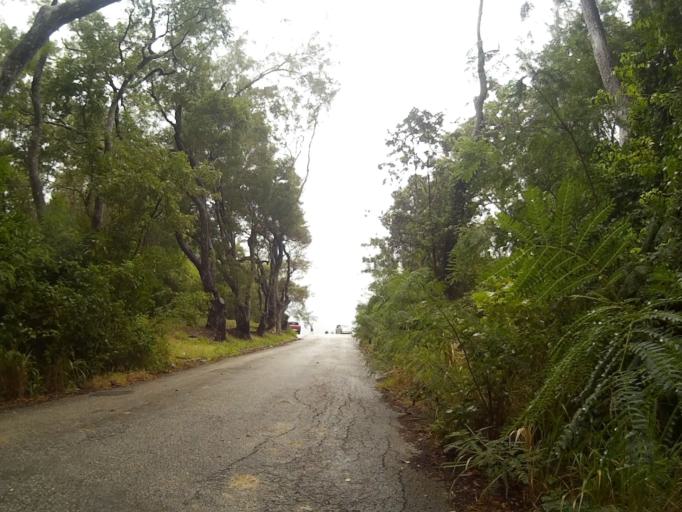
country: BB
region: Saint Andrew
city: Greenland
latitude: 13.2739
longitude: -59.5854
